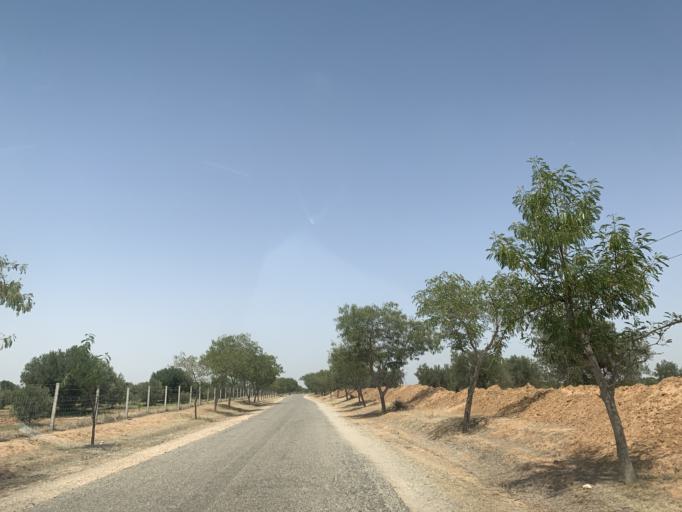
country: TN
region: Al Mahdiyah
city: Shurban
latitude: 35.1913
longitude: 10.2489
